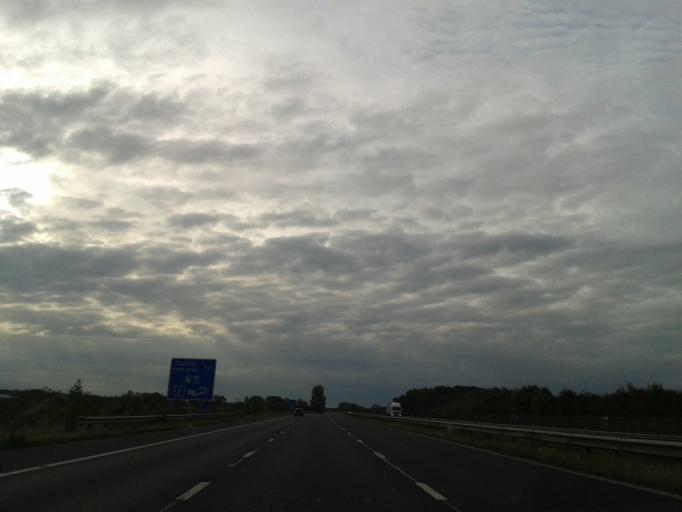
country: GB
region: Scotland
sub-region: Dumfries and Galloway
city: Gretna
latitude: 54.9623
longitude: -2.9933
